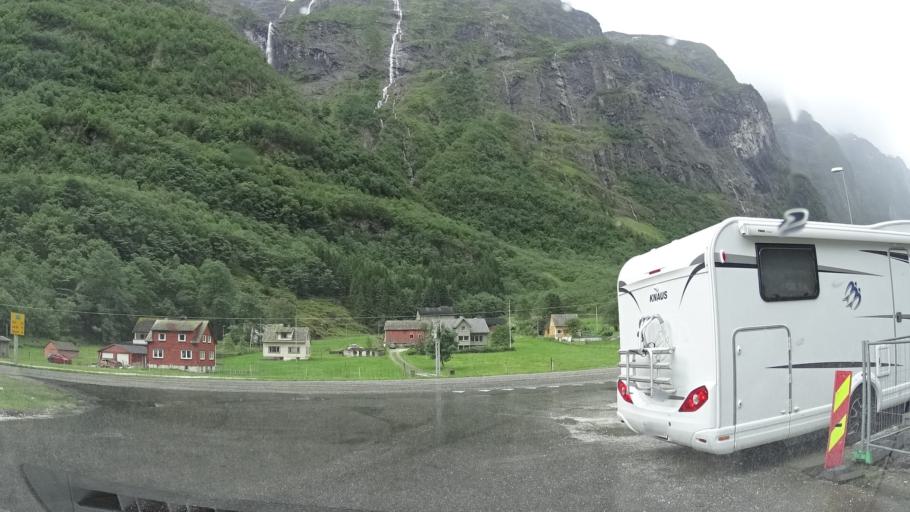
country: NO
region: Sogn og Fjordane
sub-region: Leikanger
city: Hermansverk
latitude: 60.8792
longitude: 6.8433
